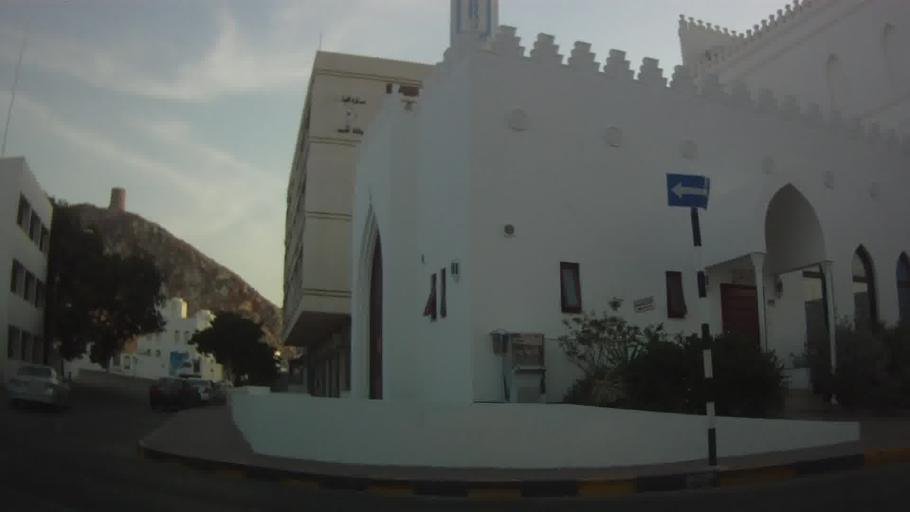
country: OM
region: Muhafazat Masqat
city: Muscat
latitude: 23.6148
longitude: 58.5902
